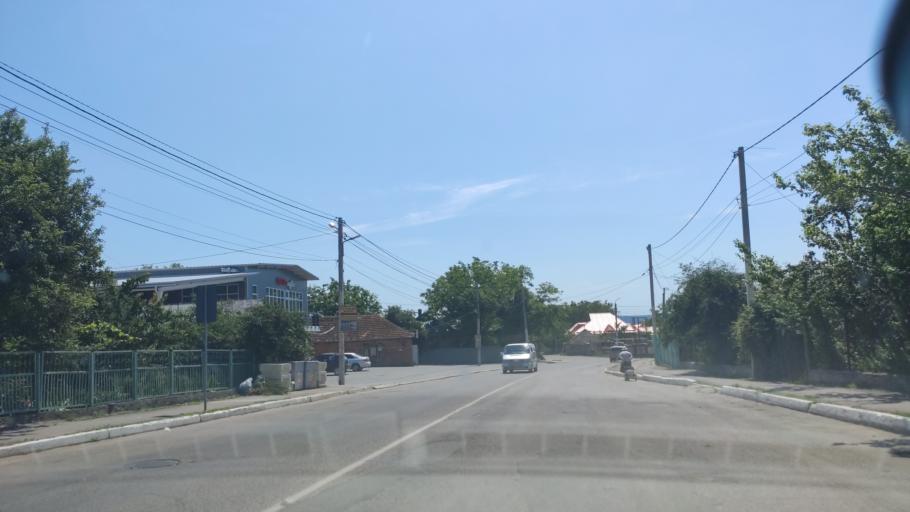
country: MD
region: Raionul Soroca
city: Soroca
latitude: 48.1665
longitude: 28.3040
